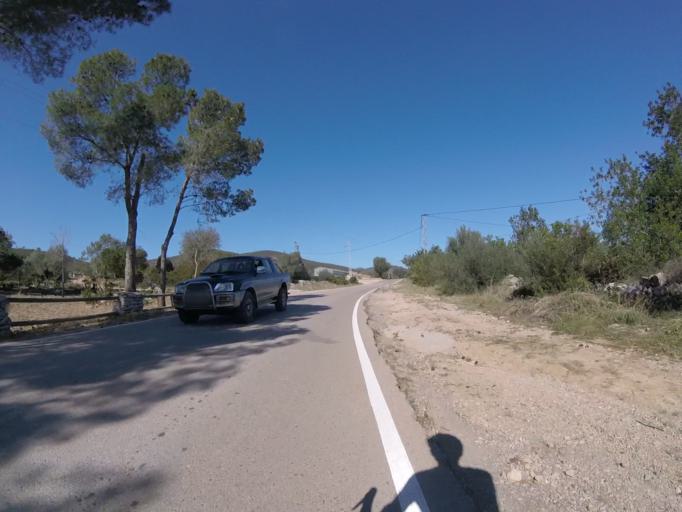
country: ES
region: Valencia
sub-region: Provincia de Castello
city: Santa Magdalena de Pulpis
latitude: 40.3613
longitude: 0.2827
